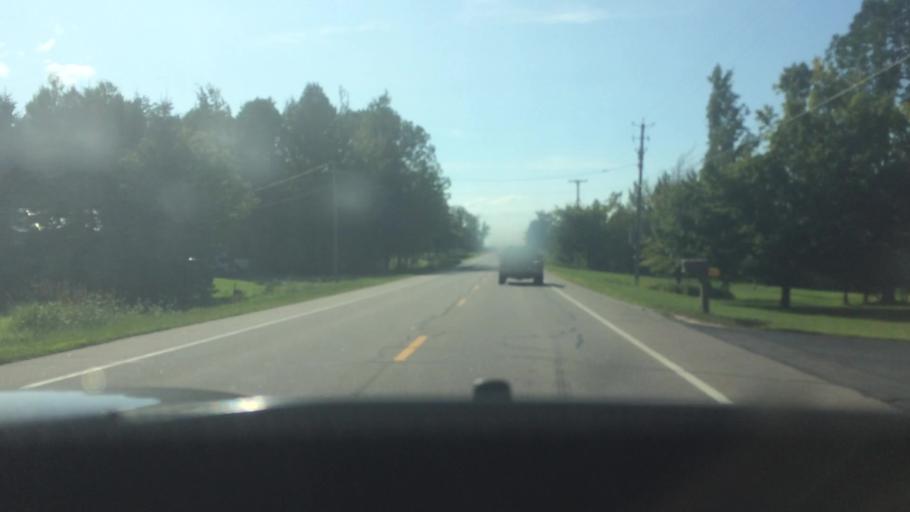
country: US
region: New York
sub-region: Franklin County
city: Malone
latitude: 44.8586
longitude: -74.2395
